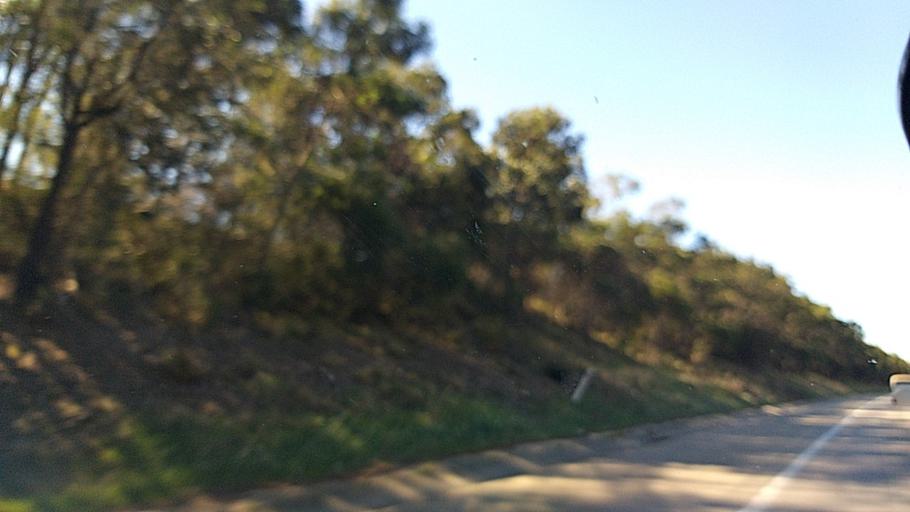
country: AU
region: New South Wales
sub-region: Wingecarribee
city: Colo Vale
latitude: -34.4223
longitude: 150.4756
